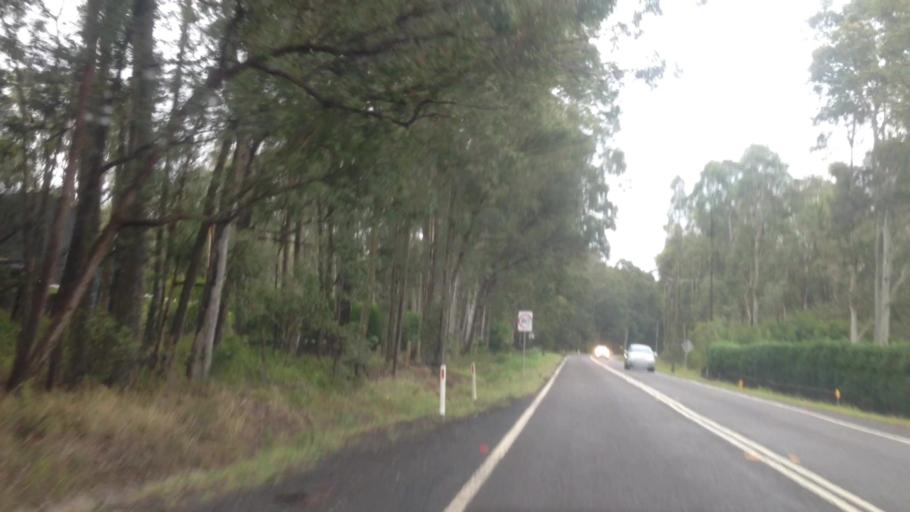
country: AU
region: New South Wales
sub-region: Wyong Shire
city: Little Jilliby
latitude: -33.2548
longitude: 151.3972
